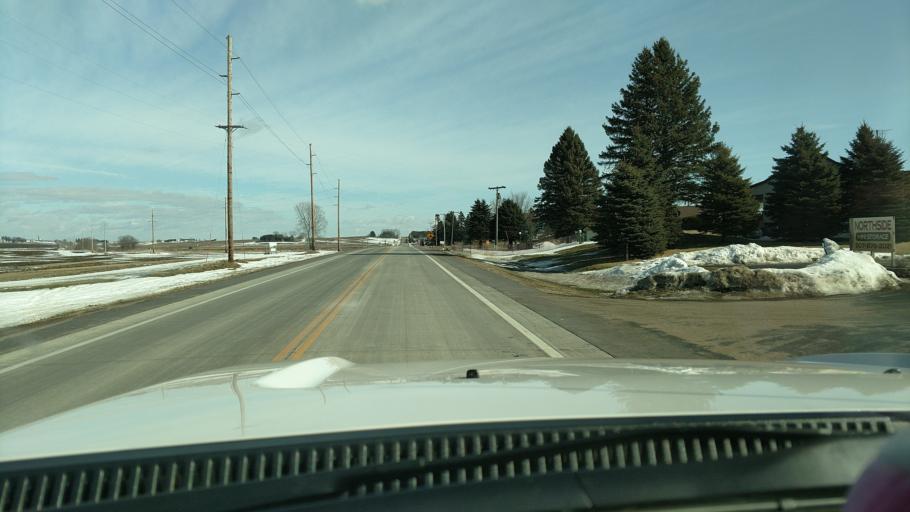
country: US
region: Minnesota
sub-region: Wabasha County
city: Elgin
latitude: 44.1364
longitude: -92.2517
